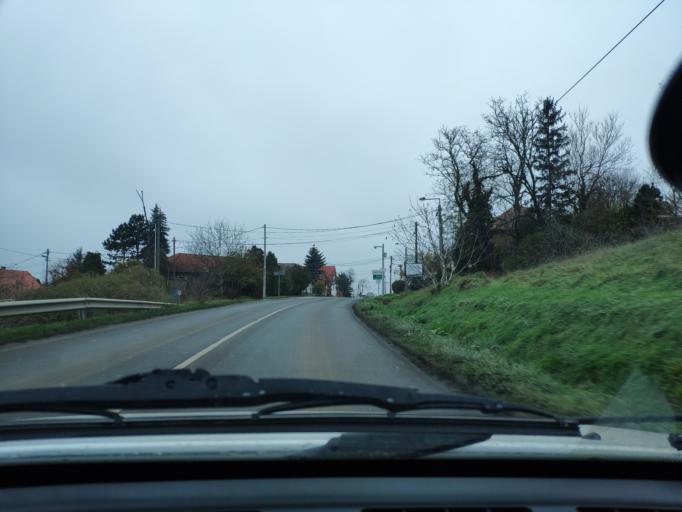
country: HU
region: Pest
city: Biatorbagy
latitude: 47.4565
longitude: 18.8128
